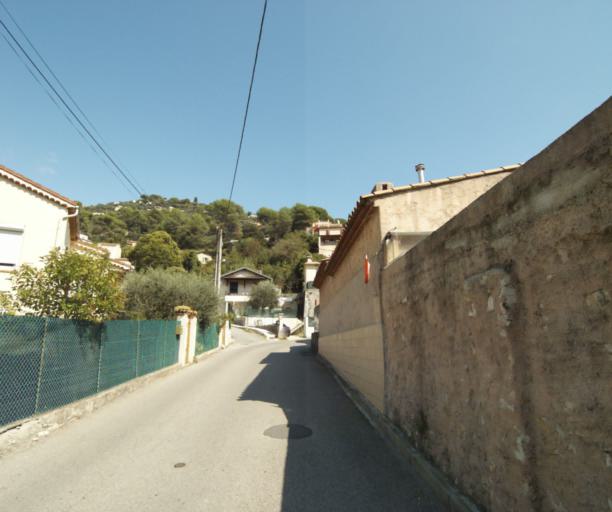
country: FR
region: Provence-Alpes-Cote d'Azur
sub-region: Departement des Alpes-Maritimes
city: Drap
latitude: 43.7568
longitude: 7.3215
